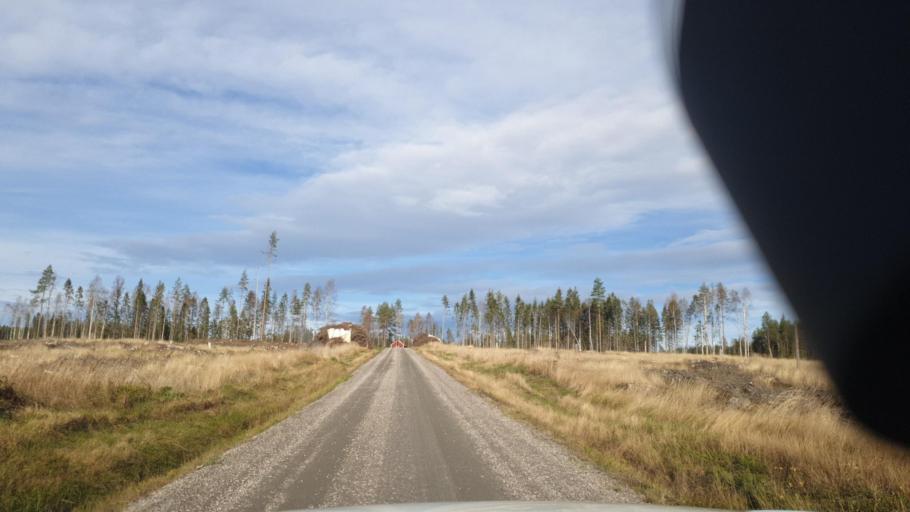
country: SE
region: Vaermland
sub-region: Eda Kommun
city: Charlottenberg
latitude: 60.0528
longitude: 12.5245
